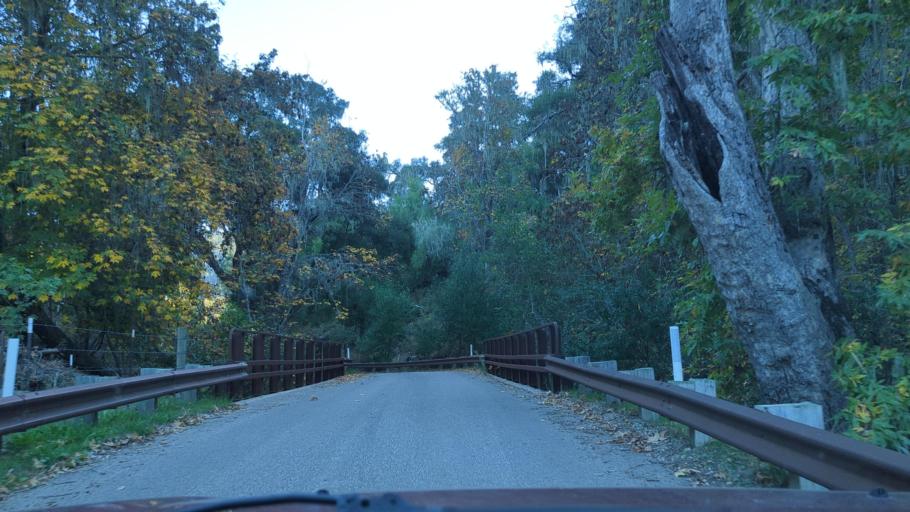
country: US
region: California
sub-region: Santa Barbara County
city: Santa Ynez
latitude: 34.5594
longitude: -120.0846
